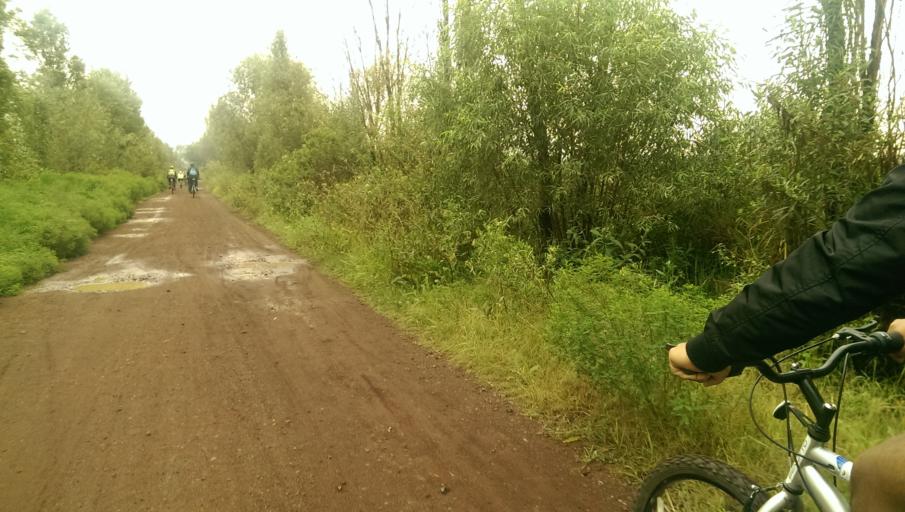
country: MX
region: Mexico City
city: Xochimilco
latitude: 19.2764
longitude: -99.0769
